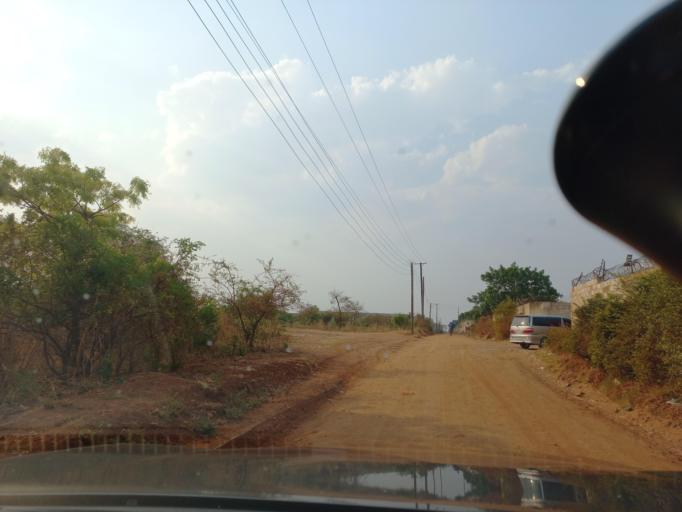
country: ZM
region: Lusaka
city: Lusaka
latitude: -15.4751
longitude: 28.2038
